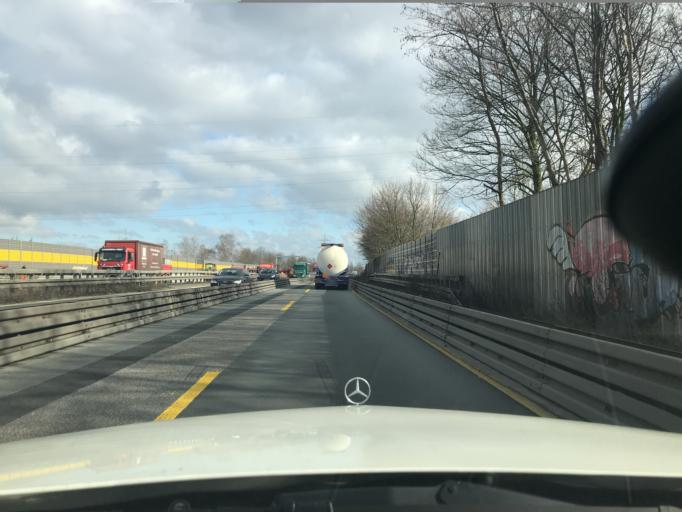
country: DE
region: North Rhine-Westphalia
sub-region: Regierungsbezirk Dusseldorf
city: Essen
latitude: 51.5127
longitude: 7.0283
